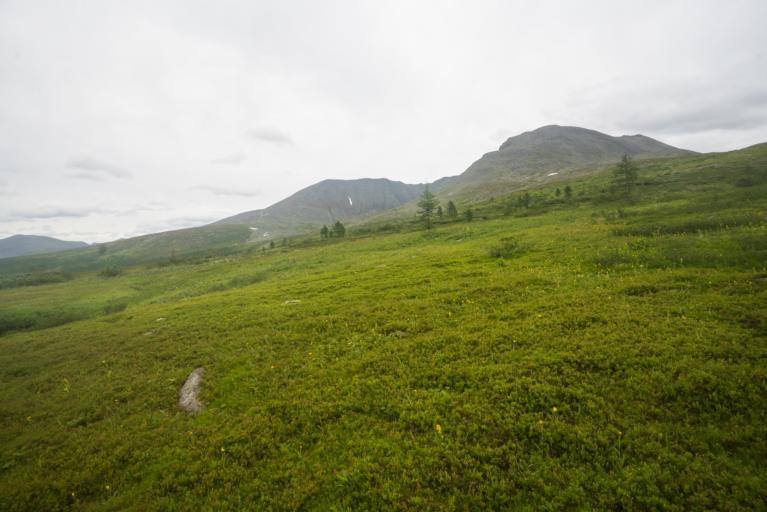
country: RU
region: Komi Republic
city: Synya
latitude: 64.8072
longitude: 59.1367
